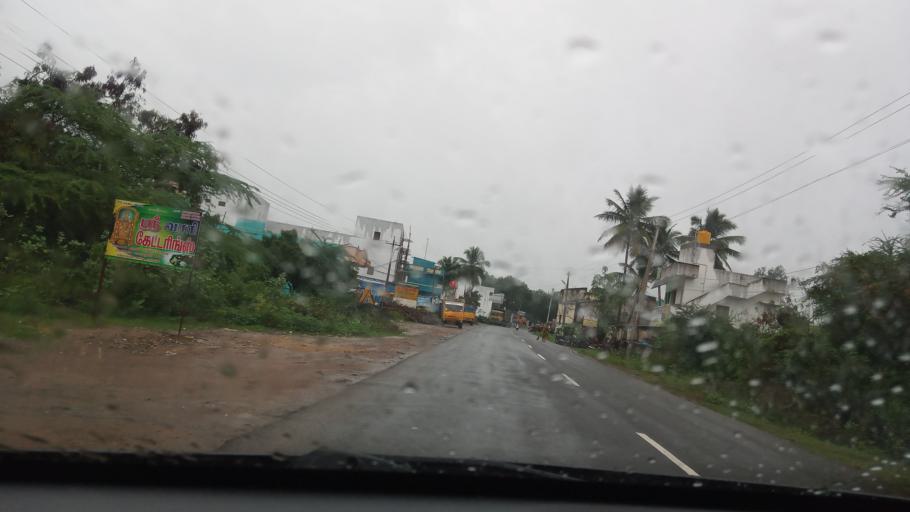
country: IN
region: Tamil Nadu
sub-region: Tiruvannamalai
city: Cheyyar
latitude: 12.6748
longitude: 79.5361
